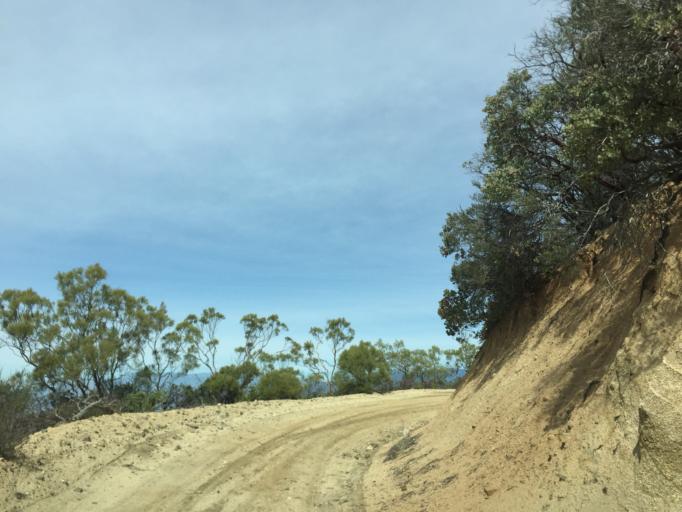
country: US
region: California
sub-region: Riverside County
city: Valle Vista
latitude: 33.6204
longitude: -116.8168
